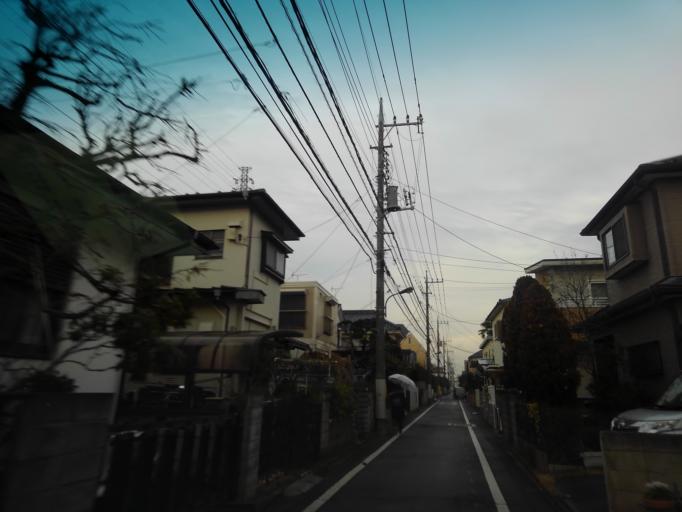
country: JP
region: Tokyo
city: Kokubunji
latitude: 35.7154
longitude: 139.4438
